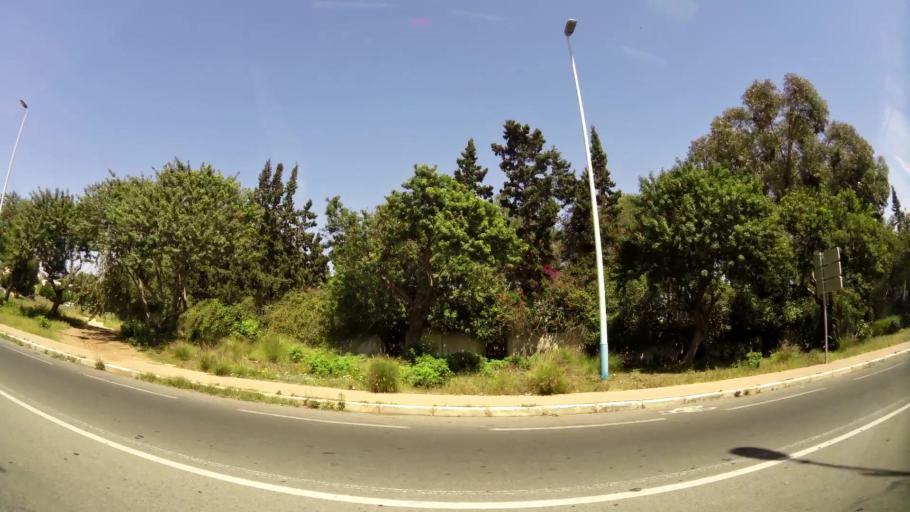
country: MA
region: Souss-Massa-Draa
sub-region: Agadir-Ida-ou-Tnan
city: Agadir
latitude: 30.4363
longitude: -9.5962
